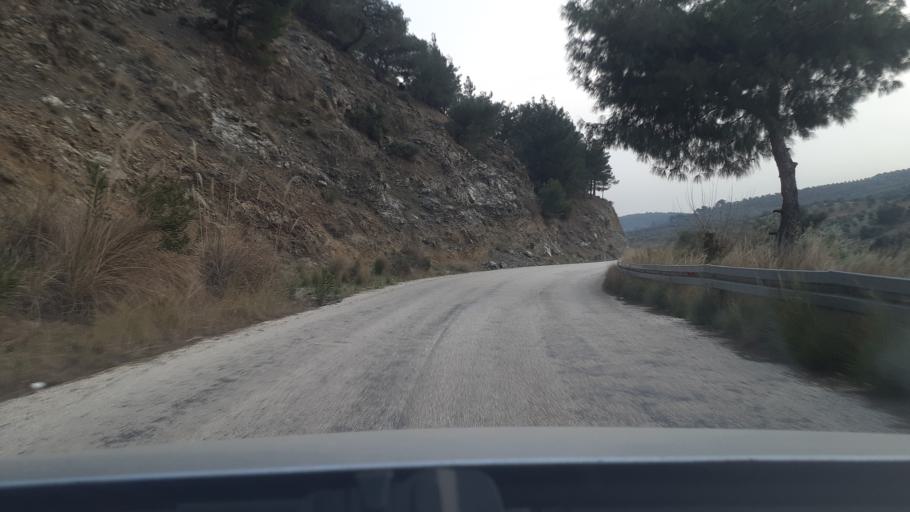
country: TR
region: Hatay
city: Kirikhan
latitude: 36.5173
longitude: 36.3186
